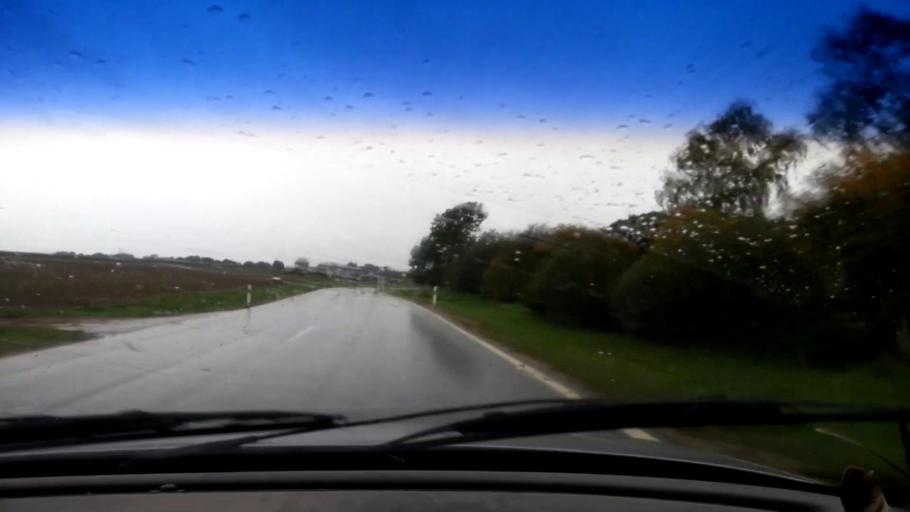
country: DE
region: Bavaria
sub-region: Upper Franconia
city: Schesslitz
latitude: 49.9644
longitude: 11.0121
